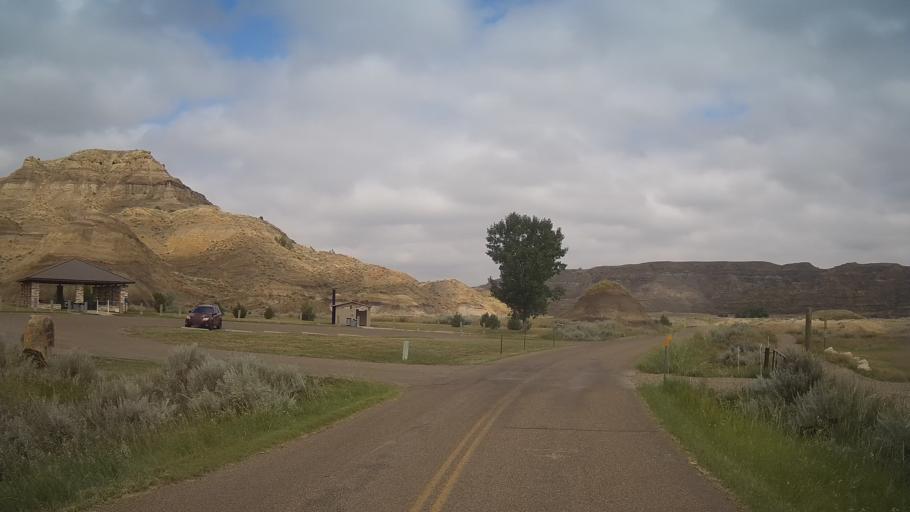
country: US
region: Montana
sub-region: Dawson County
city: Glendive
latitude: 47.0808
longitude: -104.6978
